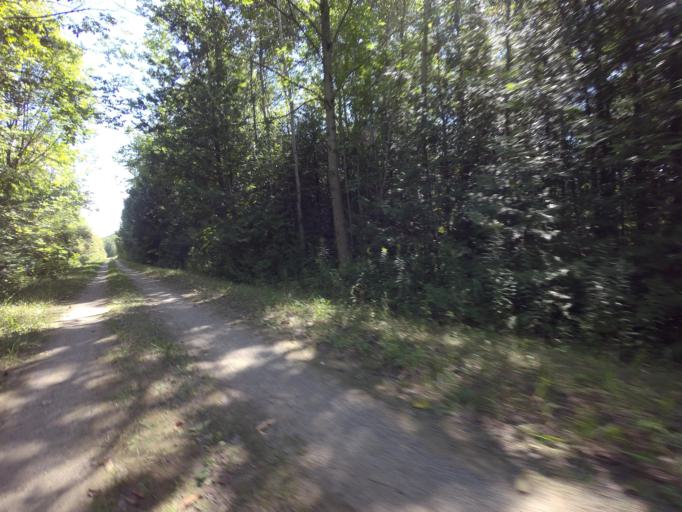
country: CA
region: Ontario
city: Orangeville
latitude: 43.7743
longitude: -80.1944
